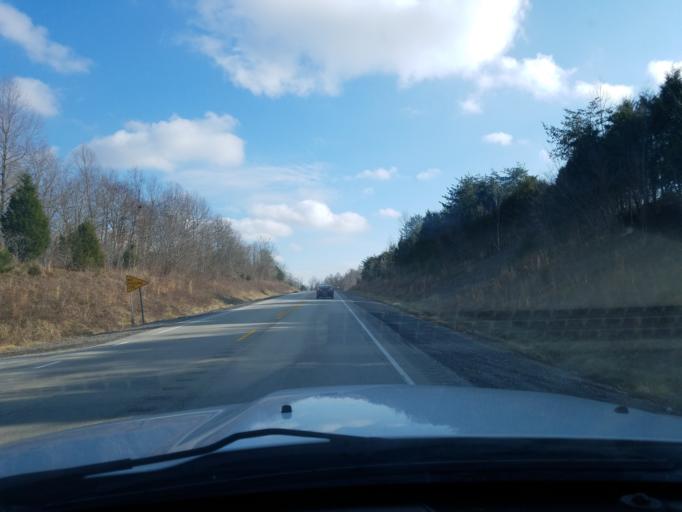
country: US
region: Kentucky
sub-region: Larue County
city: Hodgenville
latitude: 37.4727
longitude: -85.6067
